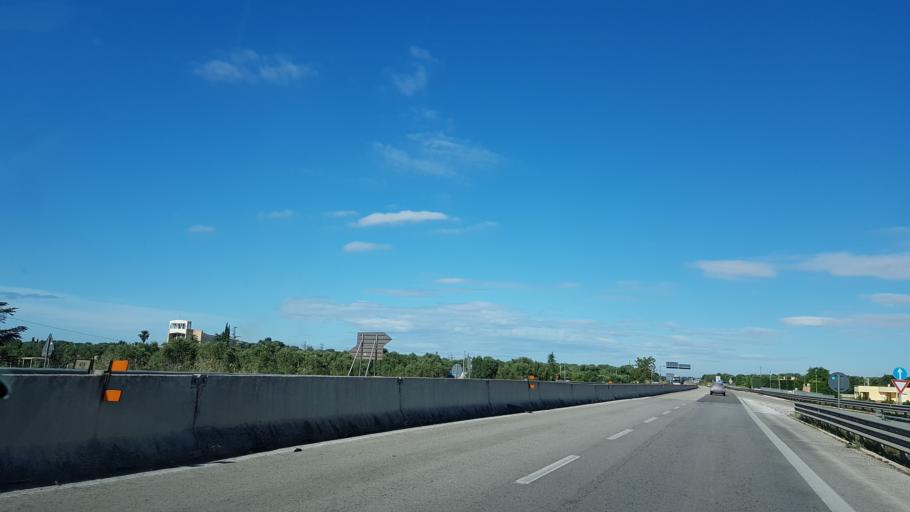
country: IT
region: Apulia
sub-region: Provincia di Brindisi
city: Latiano
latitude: 40.5478
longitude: 17.7014
